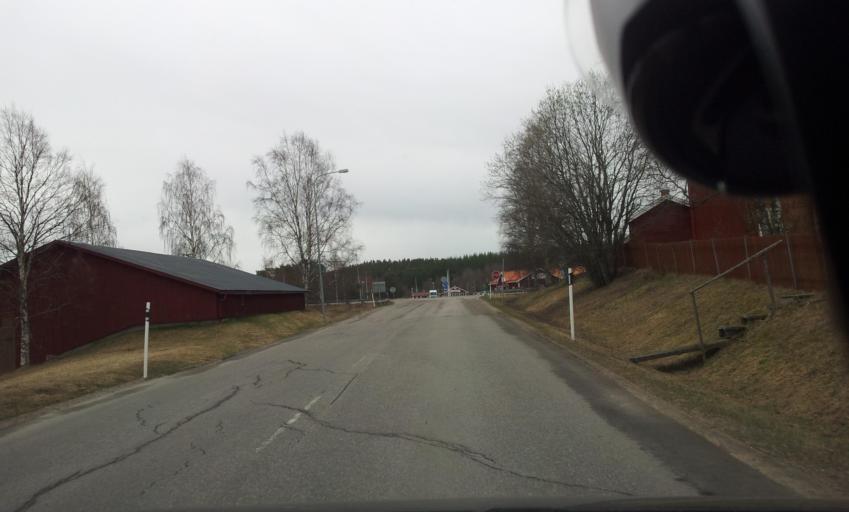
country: SE
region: Gaevleborg
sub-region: Ljusdals Kommun
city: Ljusdal
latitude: 61.8233
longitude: 16.0620
